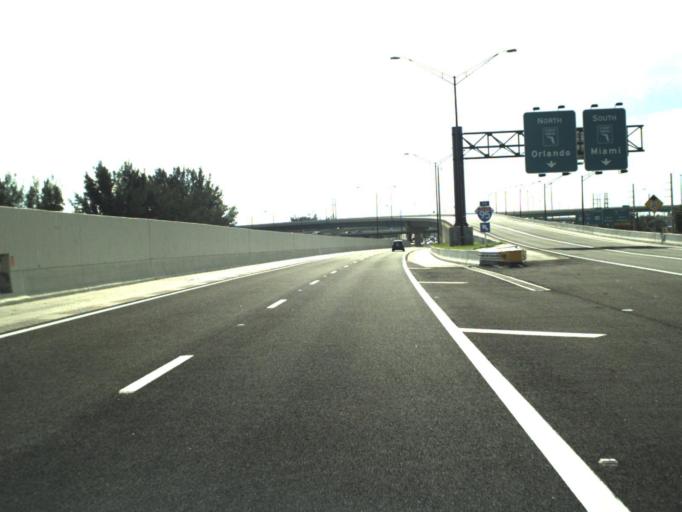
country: US
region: Florida
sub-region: Broward County
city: Broadview Park
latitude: 26.0926
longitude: -80.2231
